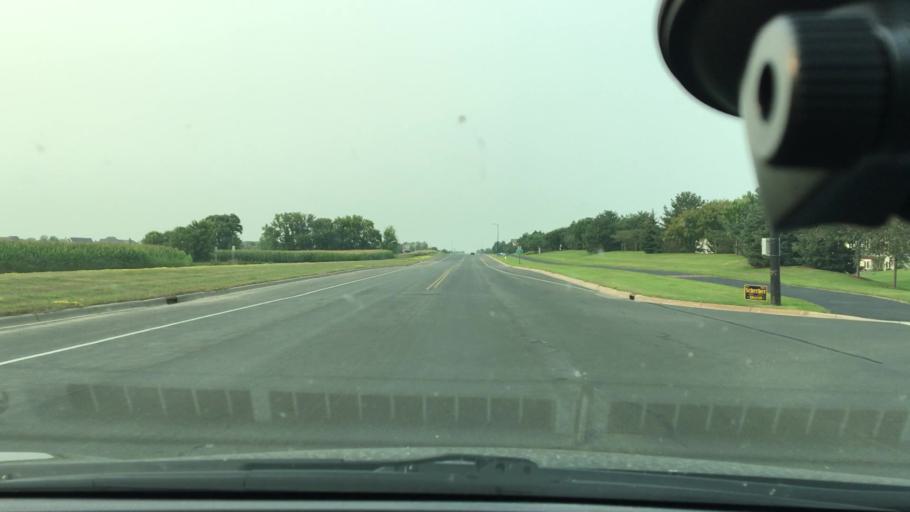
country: US
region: Minnesota
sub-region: Wright County
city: Albertville
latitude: 45.2432
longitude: -93.6428
